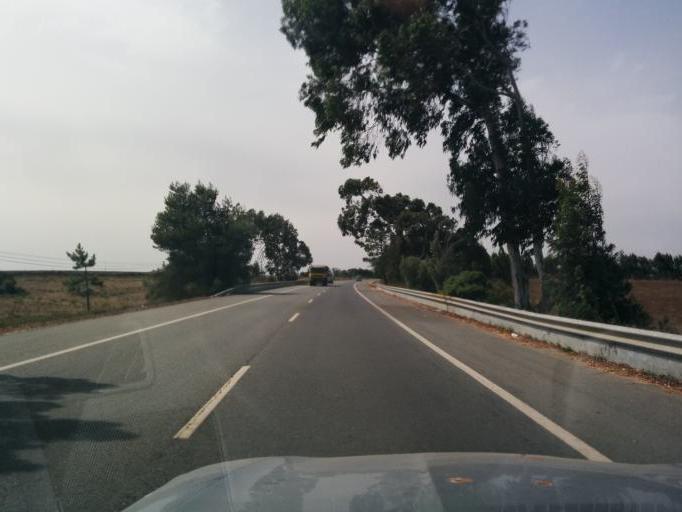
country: PT
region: Beja
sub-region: Odemira
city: Vila Nova de Milfontes
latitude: 37.7161
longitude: -8.7666
